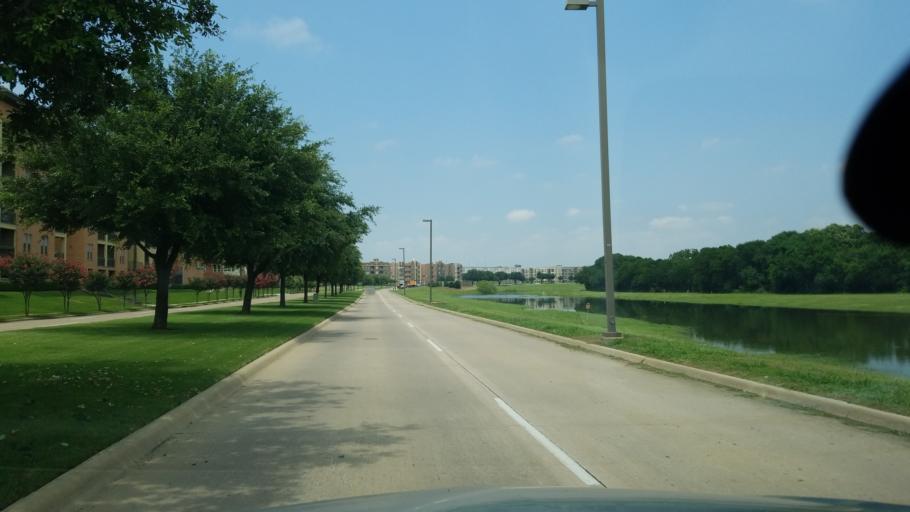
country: US
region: Texas
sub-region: Dallas County
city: Irving
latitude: 32.8680
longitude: -96.9302
